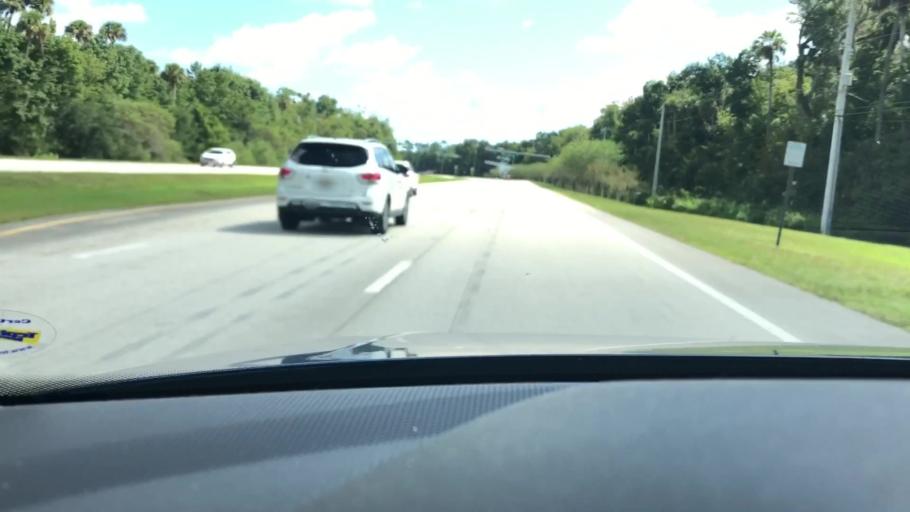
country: US
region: Florida
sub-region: Volusia County
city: Edgewater
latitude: 28.9535
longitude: -80.9378
